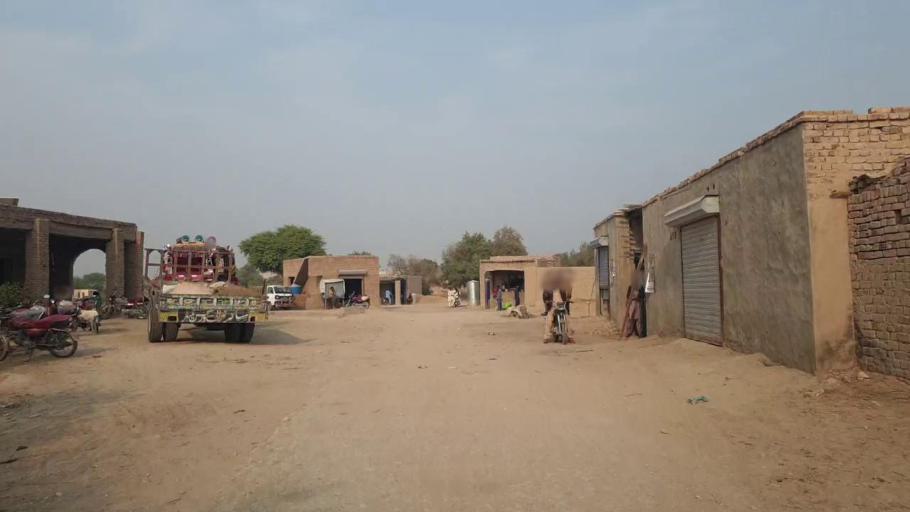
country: PK
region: Sindh
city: Sann
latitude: 26.1073
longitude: 68.0822
